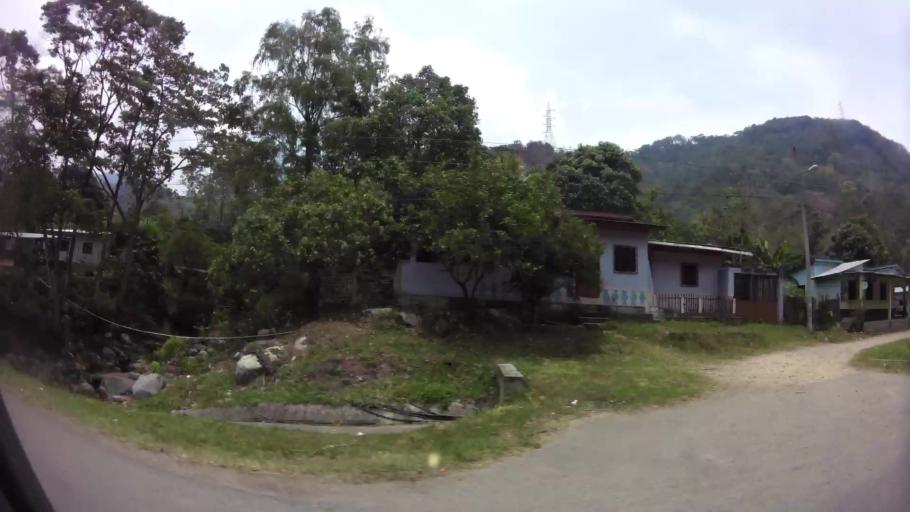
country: HN
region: Comayagua
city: Taulabe
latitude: 14.7457
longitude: -87.9608
